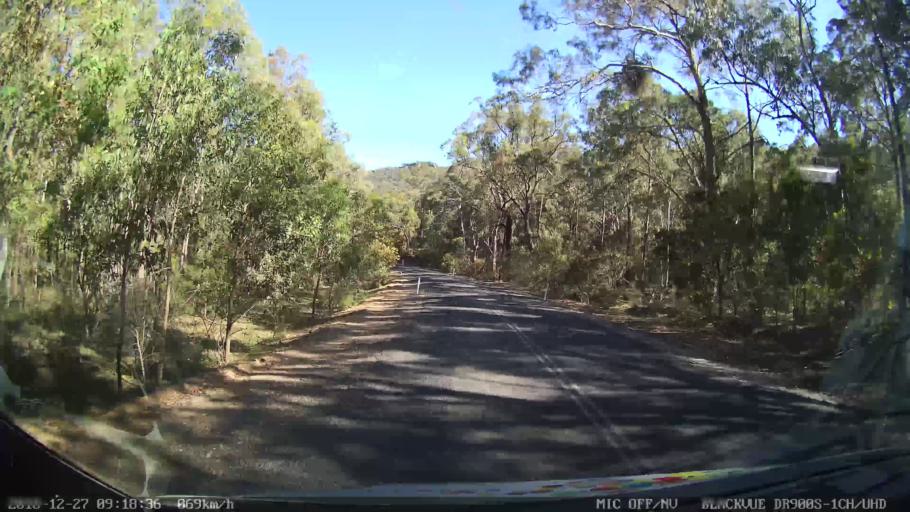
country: AU
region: New South Wales
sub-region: Lithgow
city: Portland
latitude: -33.1252
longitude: 150.0453
